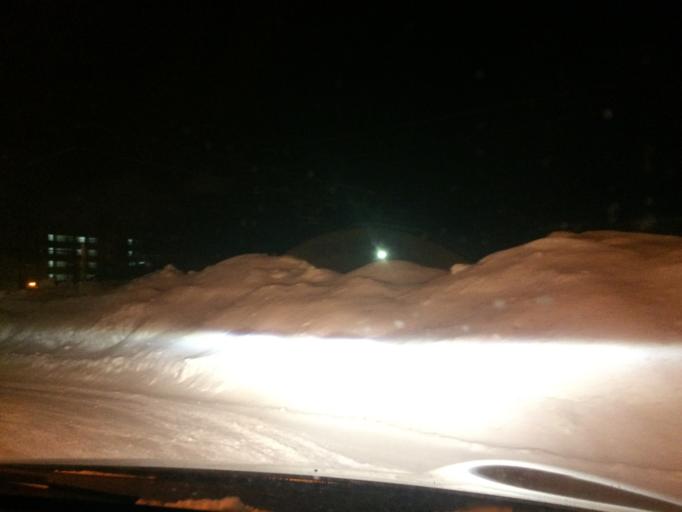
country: JP
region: Hokkaido
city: Sapporo
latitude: 43.0520
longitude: 141.4191
